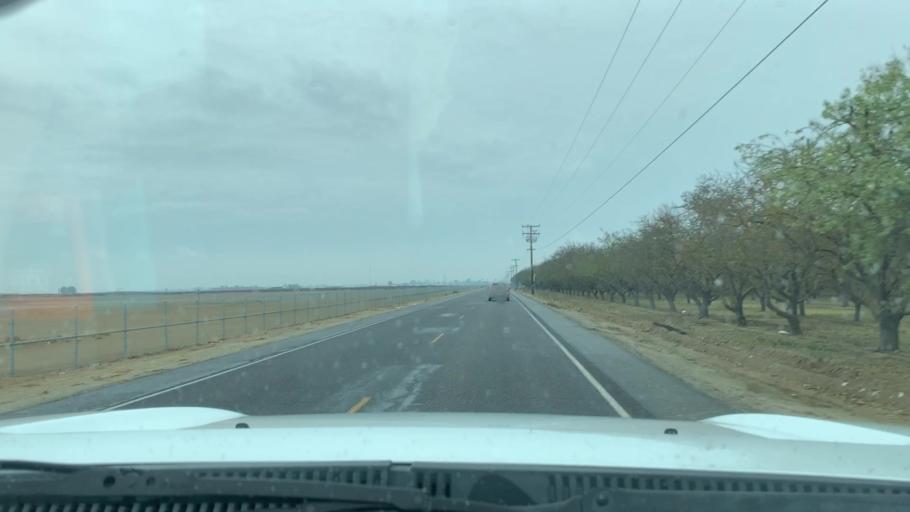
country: US
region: California
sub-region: Kern County
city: Delano
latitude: 35.7613
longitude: -119.3201
